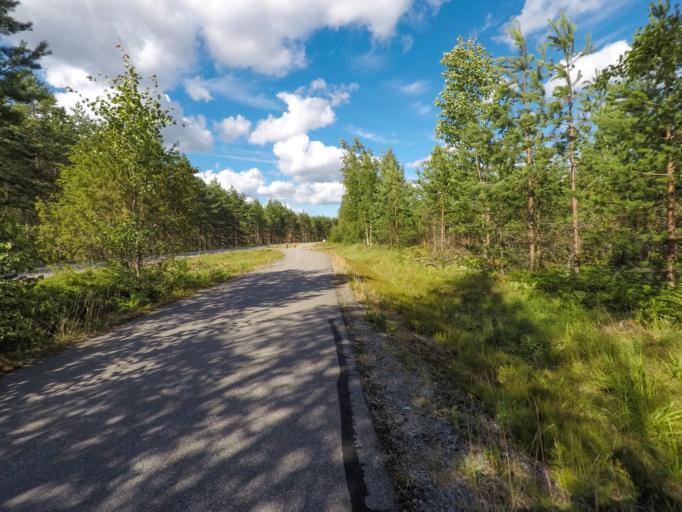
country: FI
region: South Karelia
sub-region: Lappeenranta
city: Joutseno
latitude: 61.1474
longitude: 28.5504
